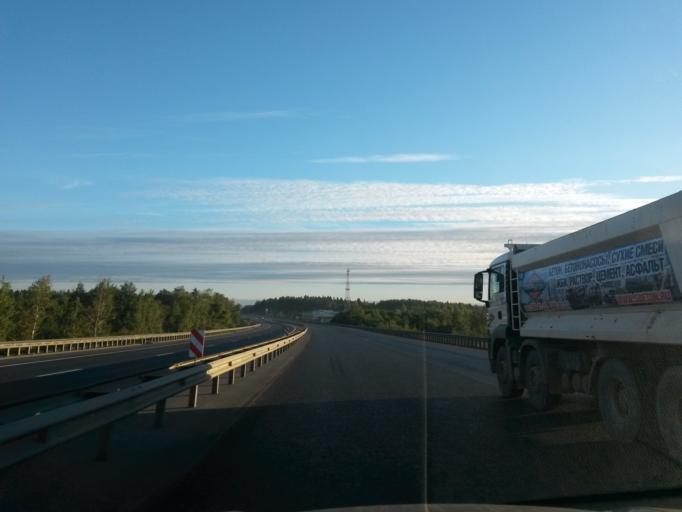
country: RU
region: Moskovskaya
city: Svatkovo
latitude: 56.3850
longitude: 38.3258
